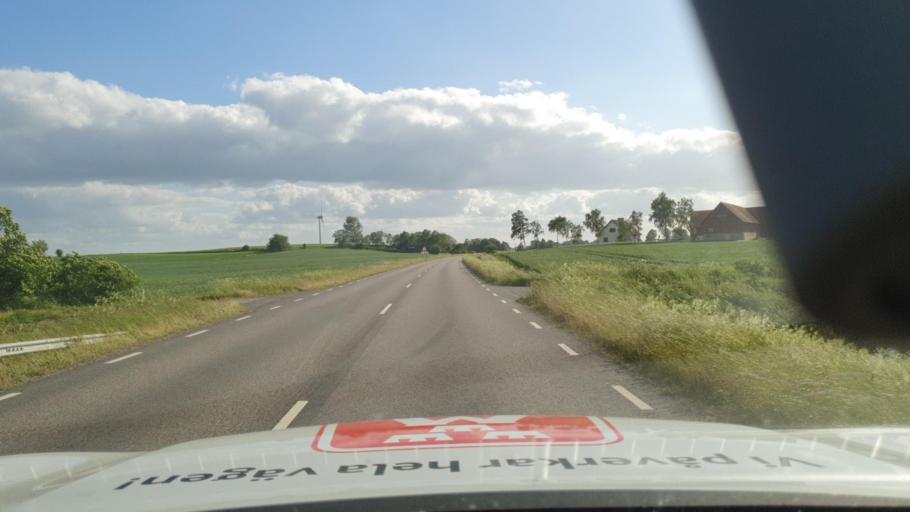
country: SE
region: Skane
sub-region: Tomelilla Kommun
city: Tomelilla
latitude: 55.5731
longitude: 13.9961
